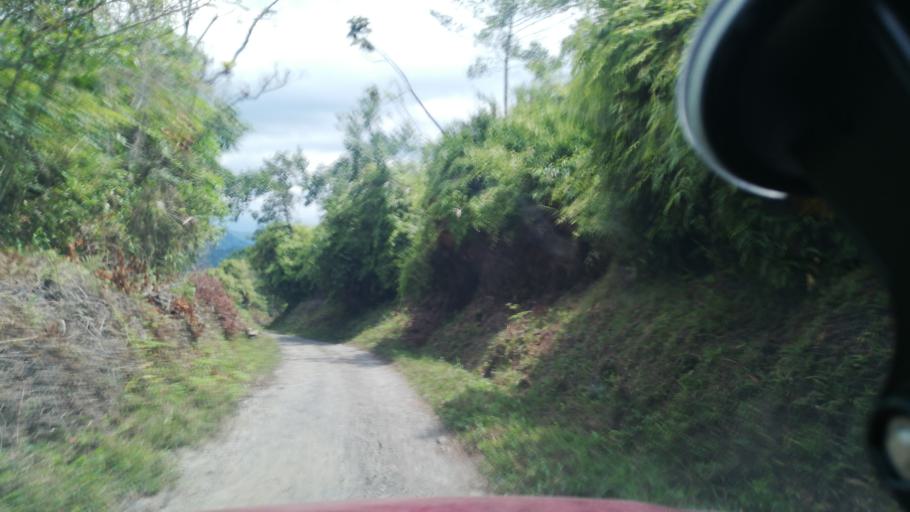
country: CO
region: Cundinamarca
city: Vergara
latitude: 5.1778
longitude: -74.2738
